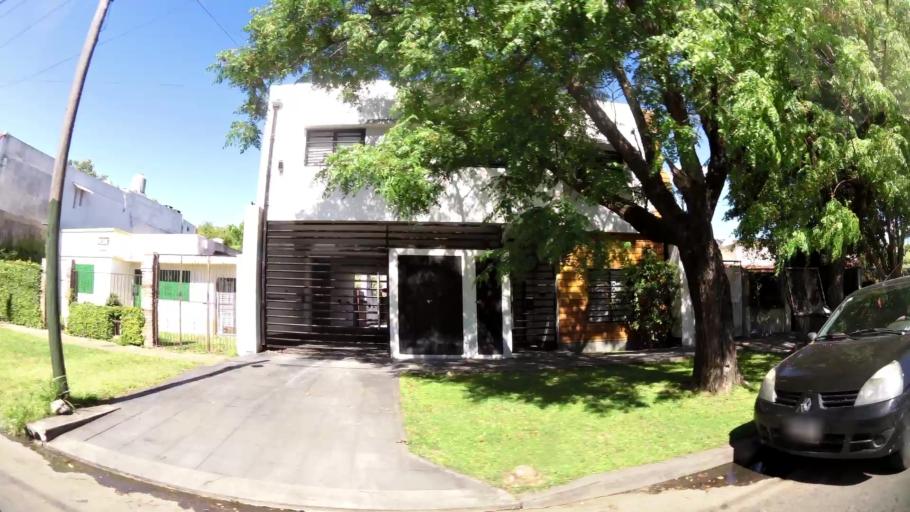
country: AR
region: Buenos Aires
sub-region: Partido de Lomas de Zamora
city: Lomas de Zamora
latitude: -34.7500
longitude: -58.4180
